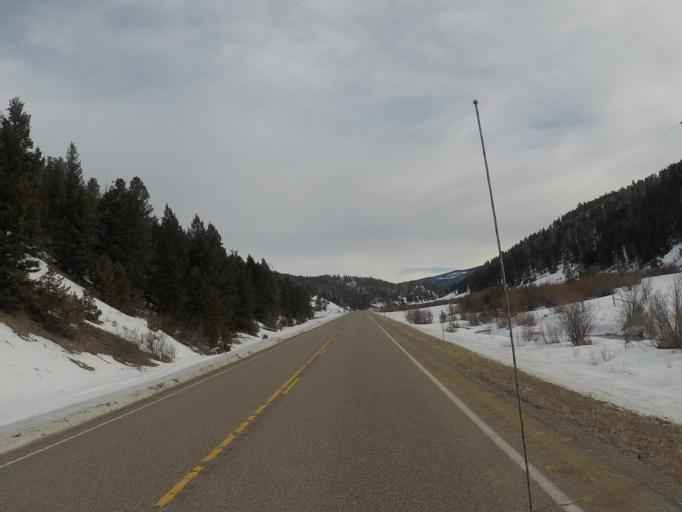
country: US
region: Montana
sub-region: Meagher County
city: White Sulphur Springs
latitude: 46.6818
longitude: -110.8756
